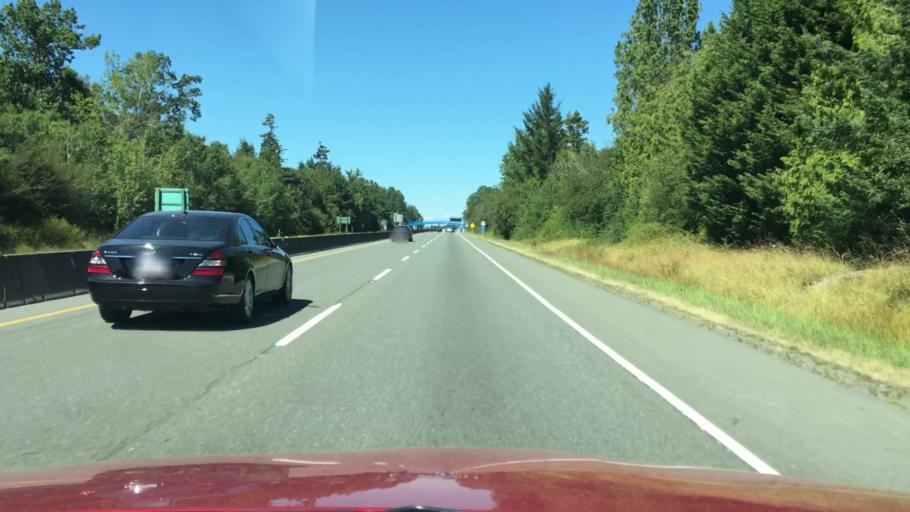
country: CA
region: British Columbia
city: North Saanich
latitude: 48.6365
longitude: -123.4092
